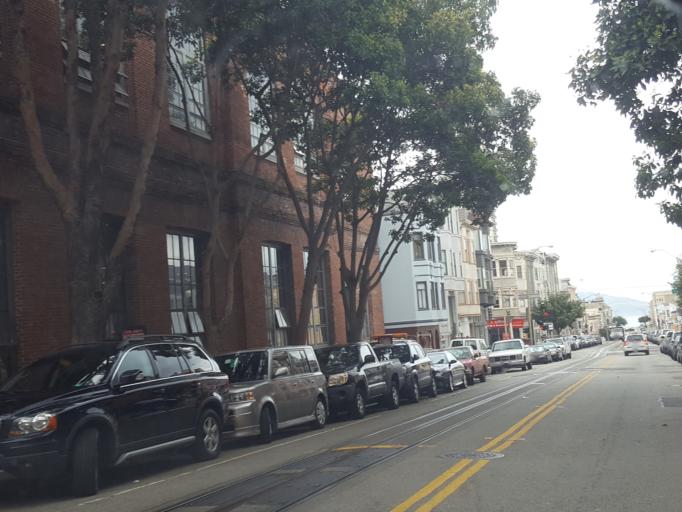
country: US
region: California
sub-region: San Francisco County
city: San Francisco
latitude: 37.7948
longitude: -122.4115
